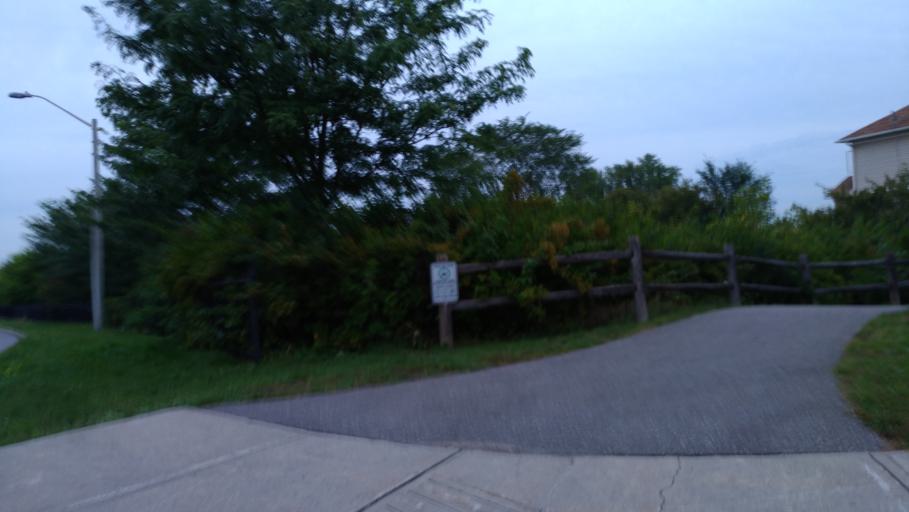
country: CA
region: Ontario
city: Bells Corners
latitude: 45.3552
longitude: -75.9348
